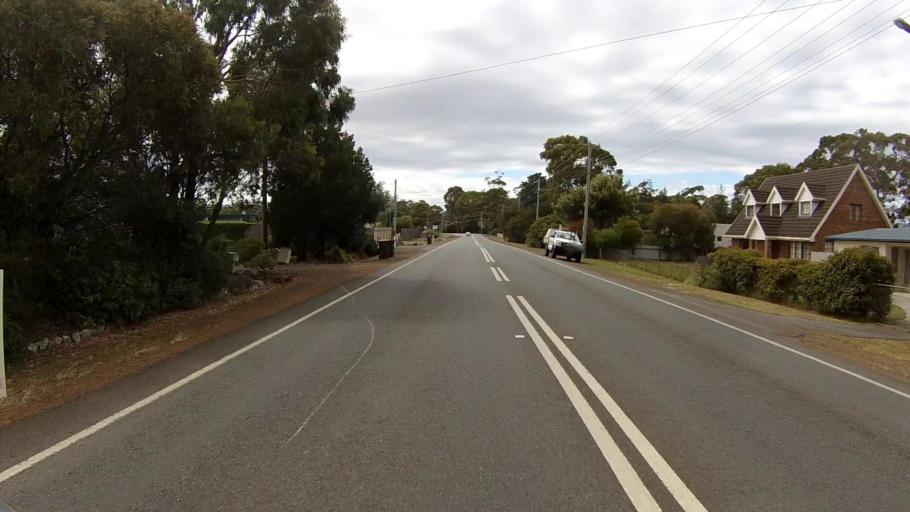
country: AU
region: Tasmania
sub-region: Sorell
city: Sorell
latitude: -42.5509
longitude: 147.8801
